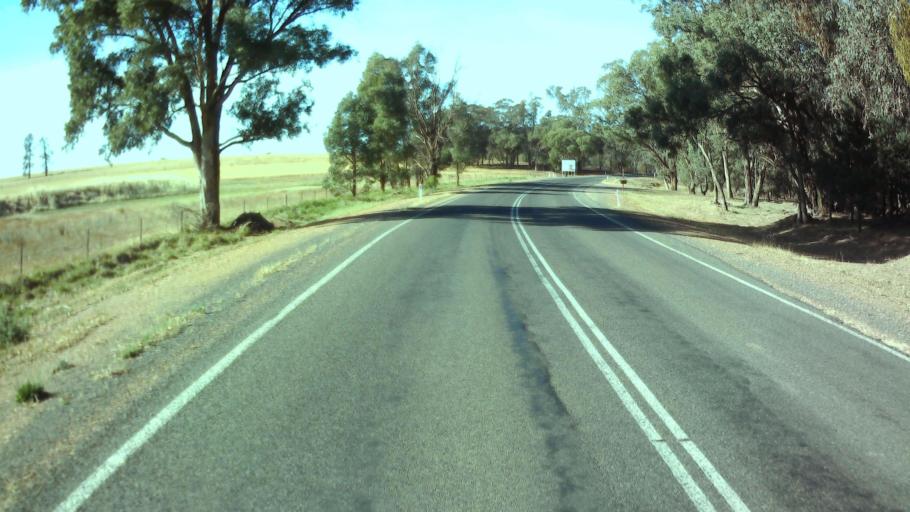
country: AU
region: New South Wales
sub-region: Weddin
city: Grenfell
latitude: -33.9981
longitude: 148.1322
